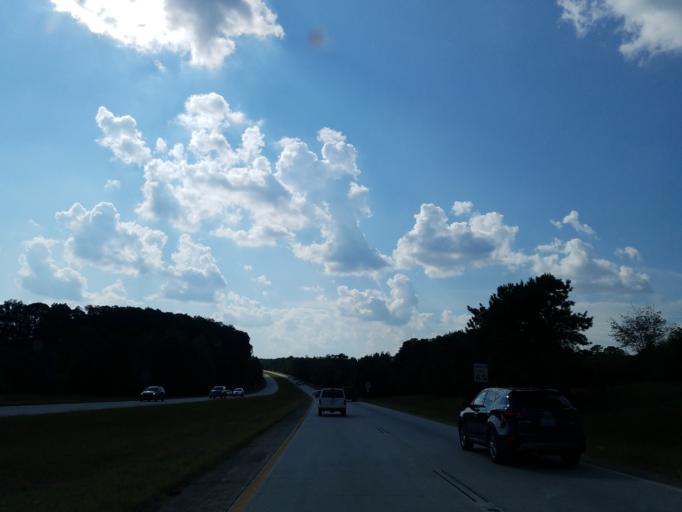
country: US
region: Georgia
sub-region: Barrow County
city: Statham
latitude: 33.9614
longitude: -83.6362
